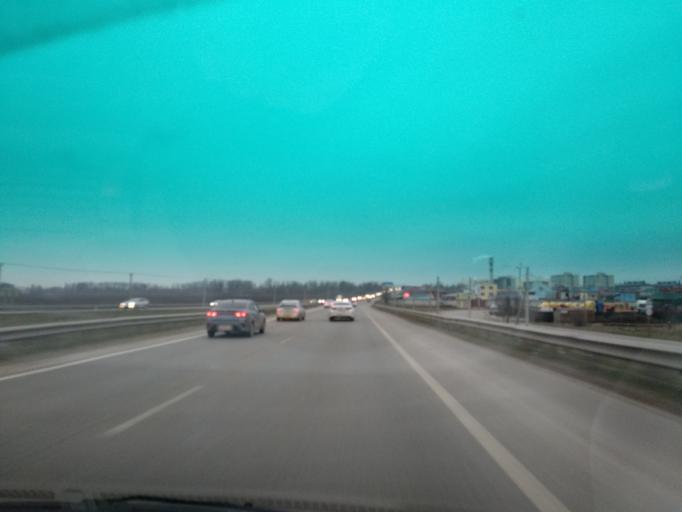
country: RU
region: Krasnodarskiy
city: Pashkovskiy
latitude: 45.0528
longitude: 39.1302
